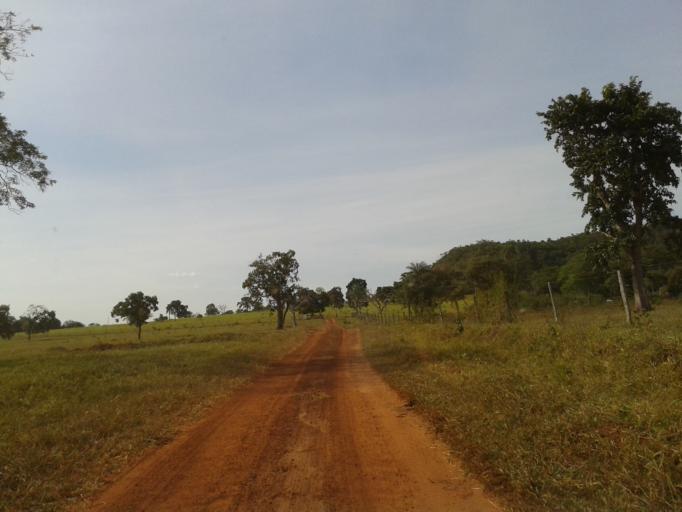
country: BR
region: Minas Gerais
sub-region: Campina Verde
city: Campina Verde
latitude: -19.5170
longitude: -49.5903
